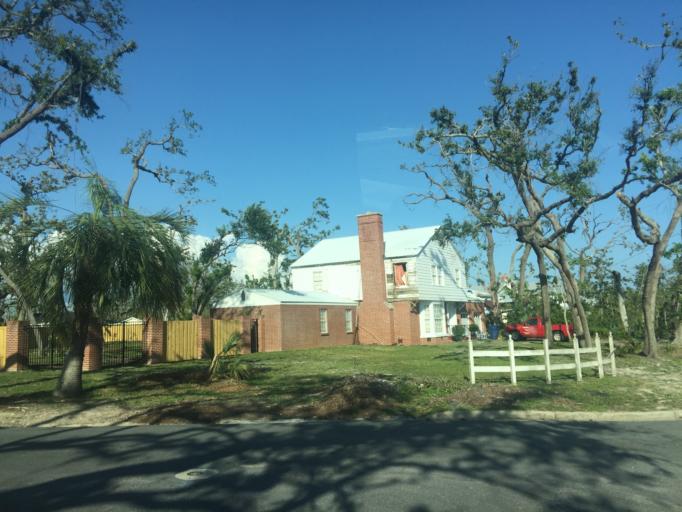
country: US
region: Florida
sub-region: Bay County
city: Panama City
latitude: 30.1441
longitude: -85.6505
